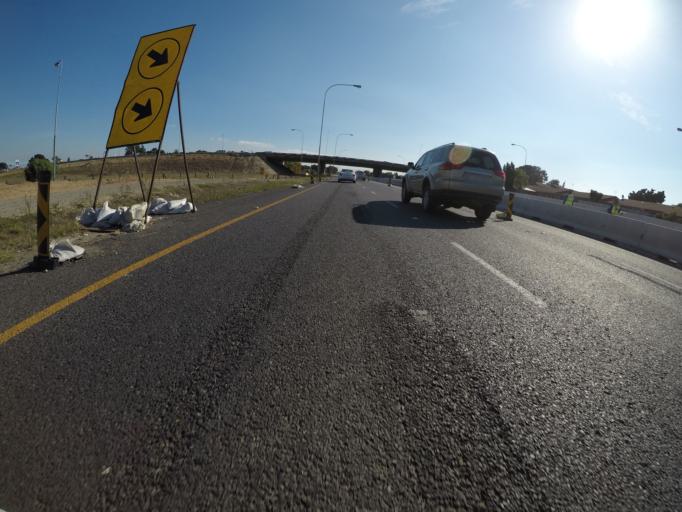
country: ZA
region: Western Cape
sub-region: City of Cape Town
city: Kraaifontein
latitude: -33.8765
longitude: 18.6603
